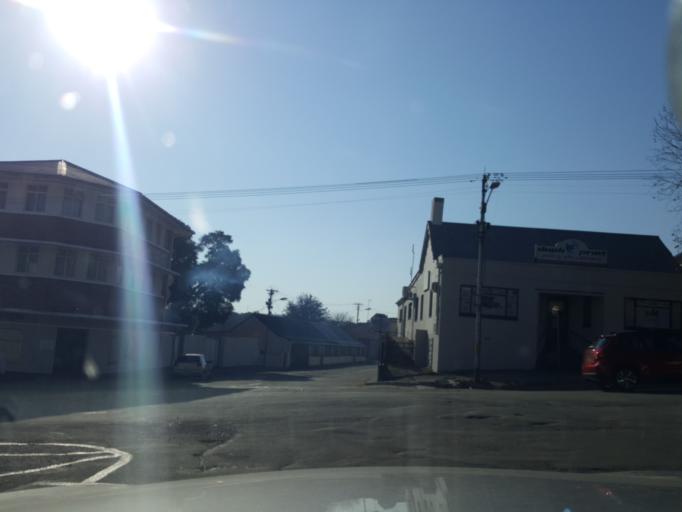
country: ZA
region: Eastern Cape
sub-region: Cacadu District Municipality
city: Grahamstown
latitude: -33.3090
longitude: 26.5254
